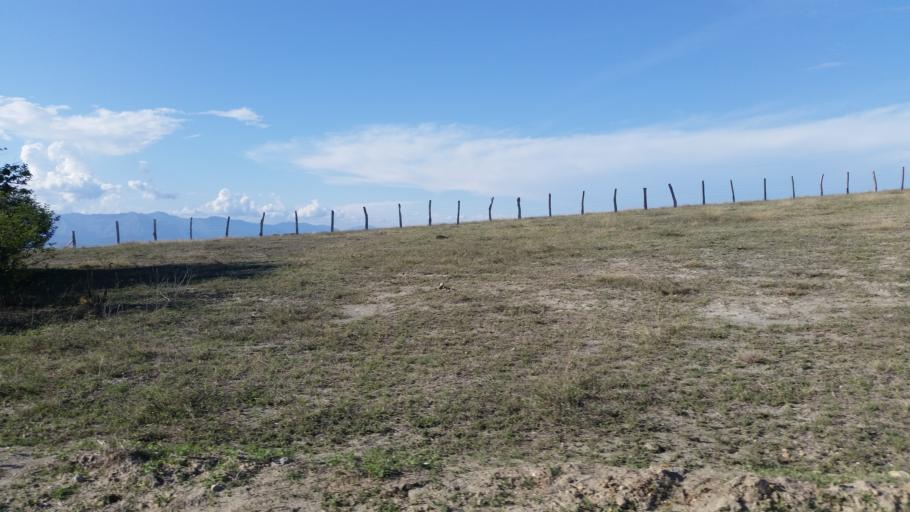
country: CO
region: Huila
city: Villavieja
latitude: 3.2332
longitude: -75.1210
